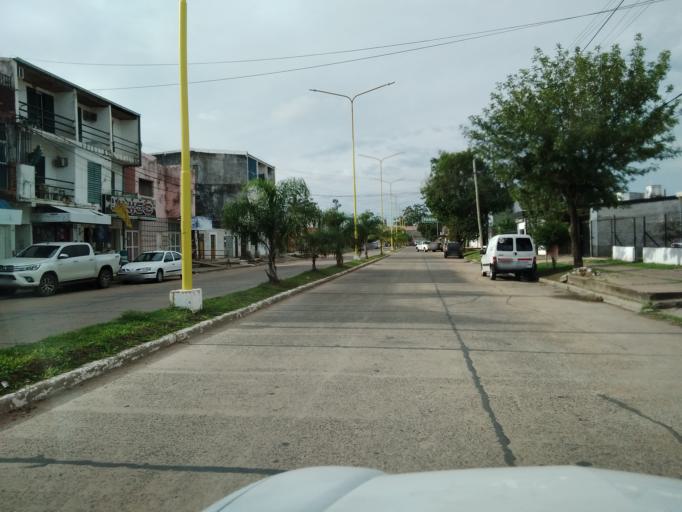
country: AR
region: Corrientes
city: Corrientes
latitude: -27.4632
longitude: -58.7877
